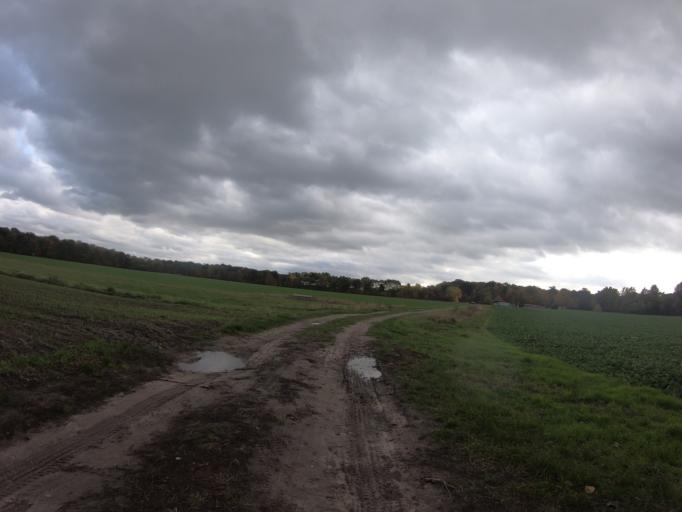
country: DE
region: Lower Saxony
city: Adenbuettel
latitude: 52.3973
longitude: 10.4826
